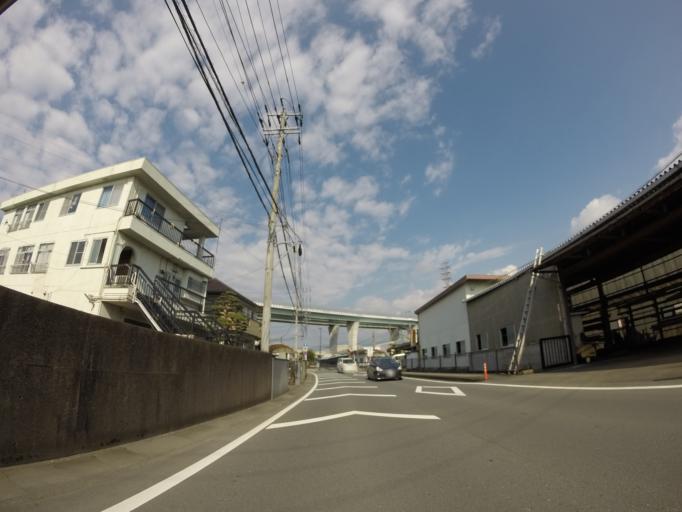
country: JP
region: Shizuoka
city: Fujinomiya
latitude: 35.1953
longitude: 138.6418
